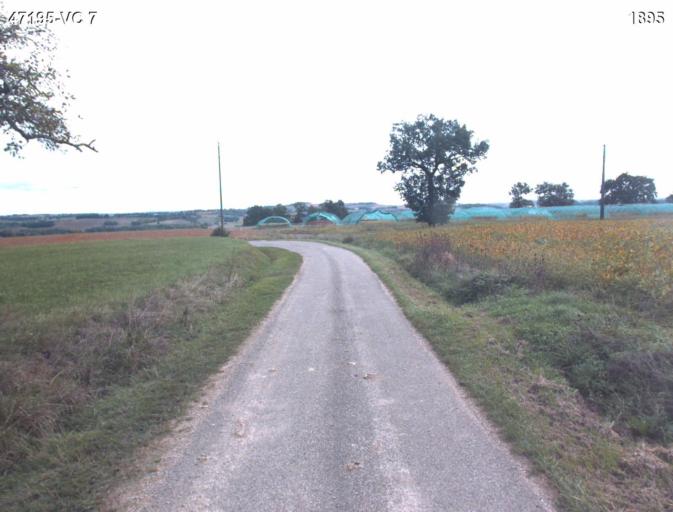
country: FR
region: Aquitaine
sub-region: Departement du Lot-et-Garonne
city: Nerac
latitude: 44.1002
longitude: 0.3397
